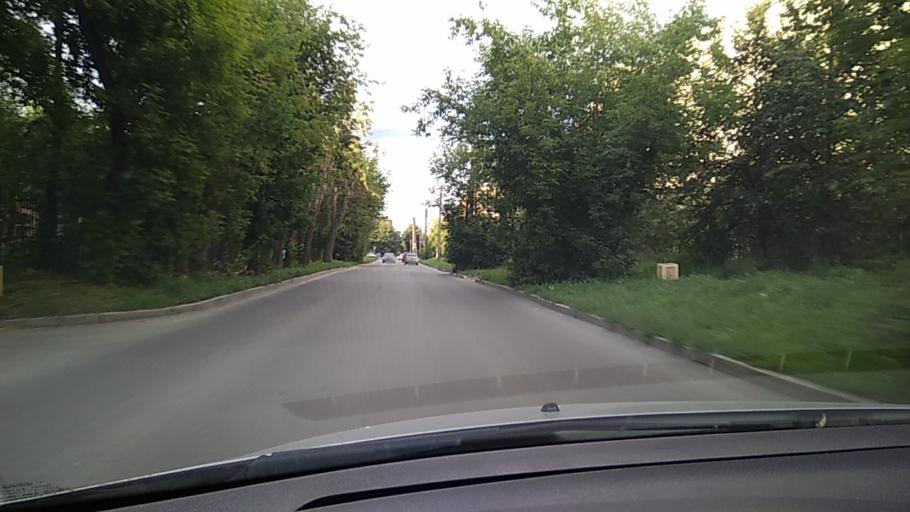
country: RU
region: Sverdlovsk
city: Yekaterinburg
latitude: 56.8950
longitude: 60.6220
